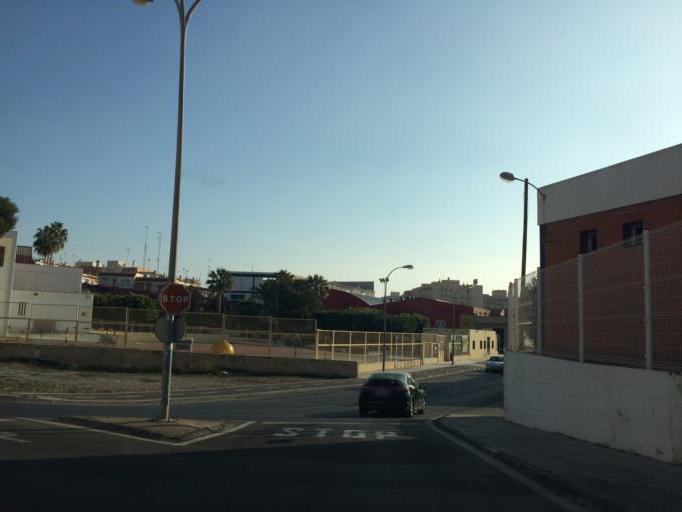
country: ES
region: Andalusia
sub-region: Provincia de Almeria
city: Almeria
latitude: 36.8528
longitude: -2.4549
